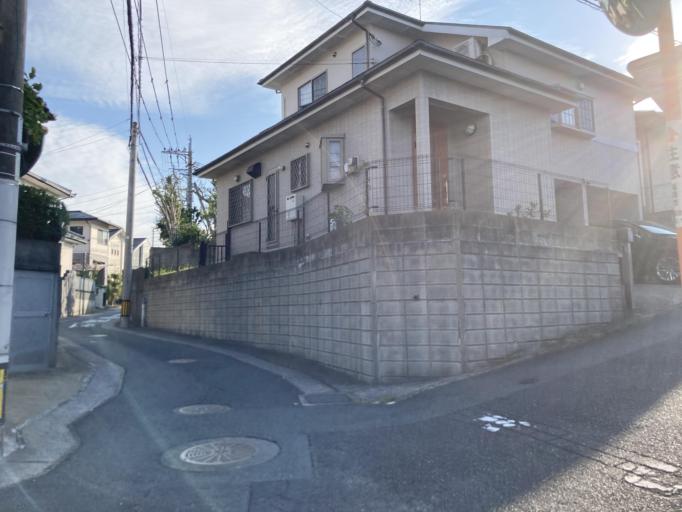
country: JP
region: Fukuoka
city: Fukuoka-shi
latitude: 33.5484
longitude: 130.3546
